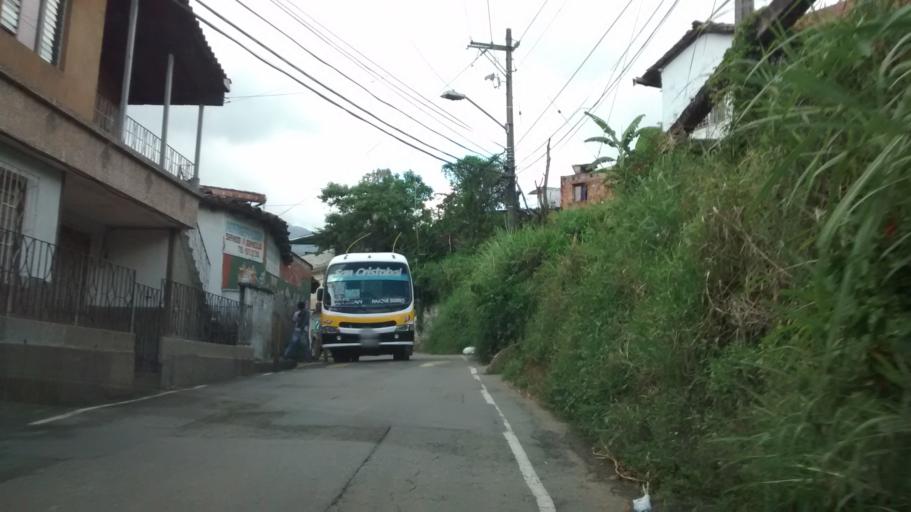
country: CO
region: Antioquia
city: Medellin
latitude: 6.2735
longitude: -75.6288
